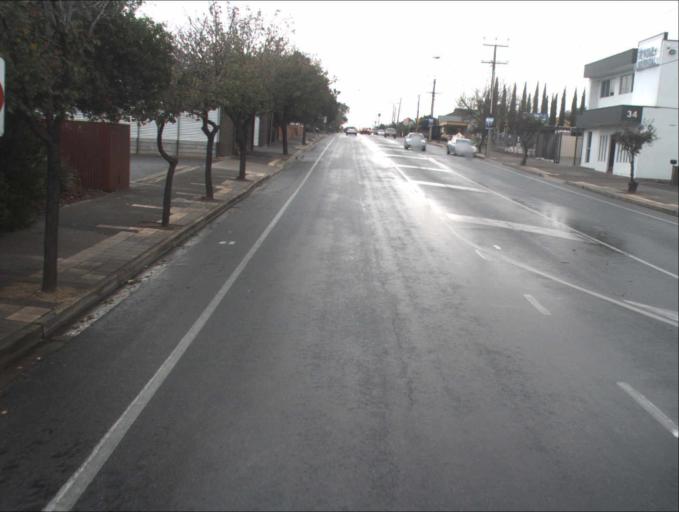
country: AU
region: South Australia
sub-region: Port Adelaide Enfield
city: Klemzig
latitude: -34.8784
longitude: 138.6347
